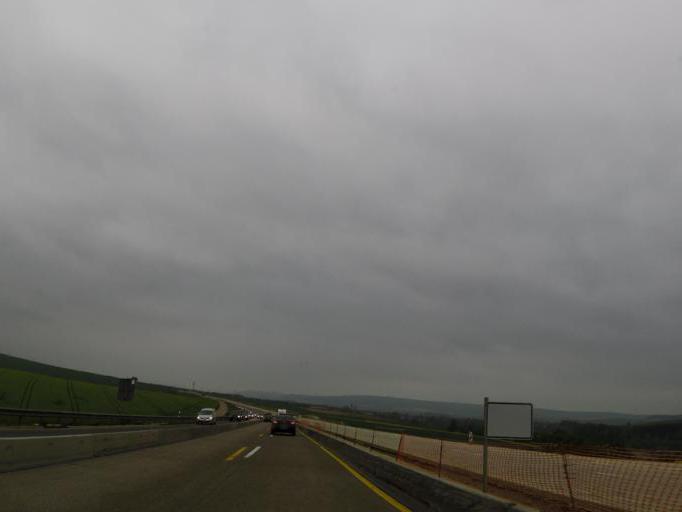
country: DE
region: Lower Saxony
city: Bockenem
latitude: 51.9633
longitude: 10.1409
